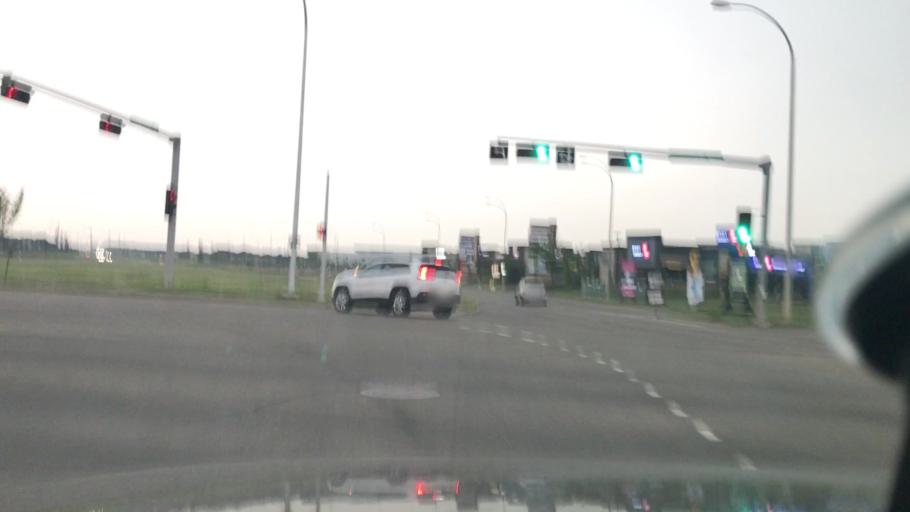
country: CA
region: Alberta
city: Devon
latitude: 53.4376
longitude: -113.6139
